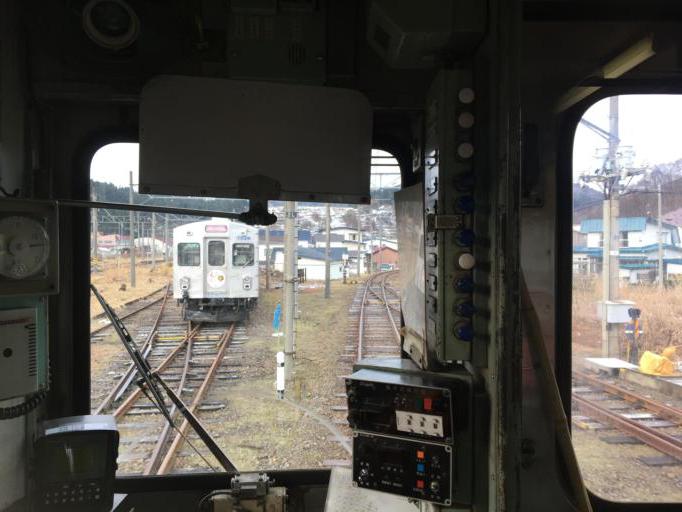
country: JP
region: Aomori
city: Hirosaki
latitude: 40.5217
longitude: 140.5661
